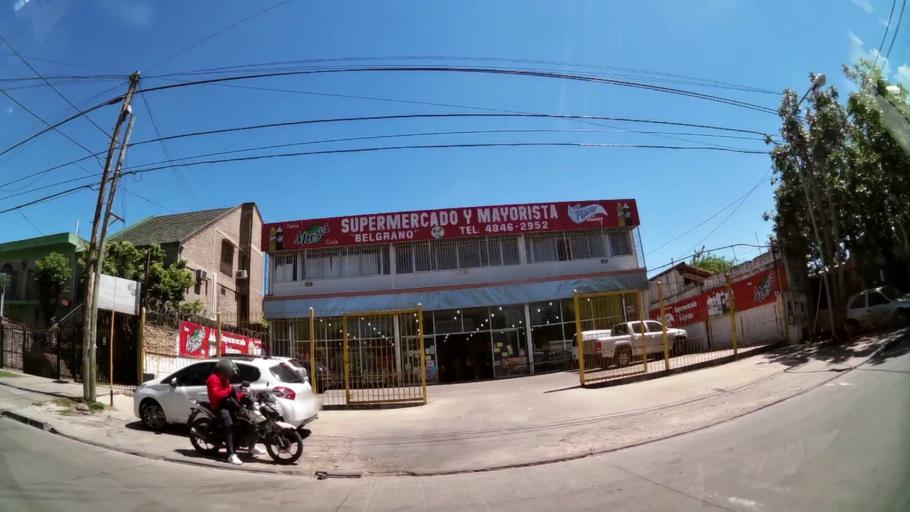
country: AR
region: Buenos Aires
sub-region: Partido de Tigre
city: Tigre
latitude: -34.4844
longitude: -58.6403
